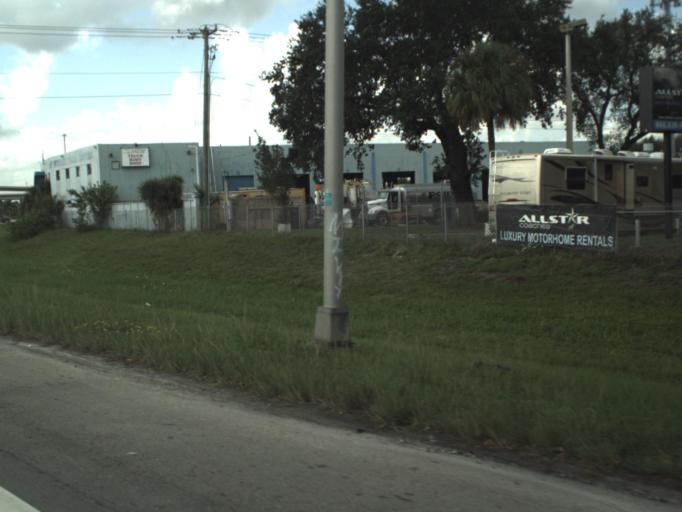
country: US
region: Florida
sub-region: Broward County
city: Broadview Park
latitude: 26.0918
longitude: -80.2012
